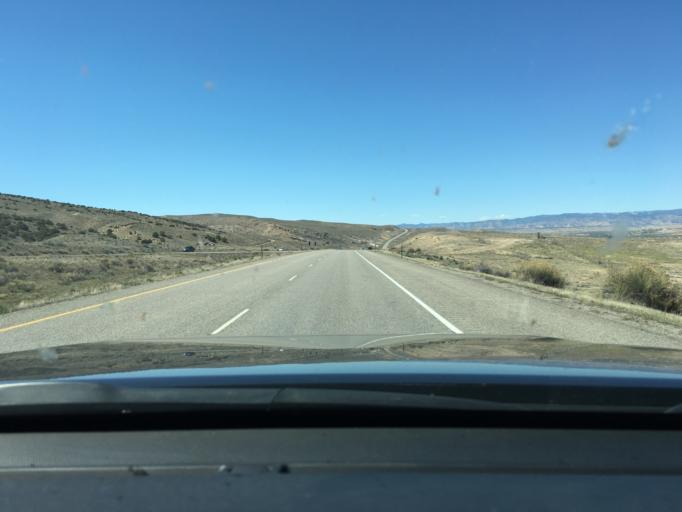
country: US
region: Colorado
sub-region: Mesa County
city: Loma
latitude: 39.2178
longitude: -108.8759
